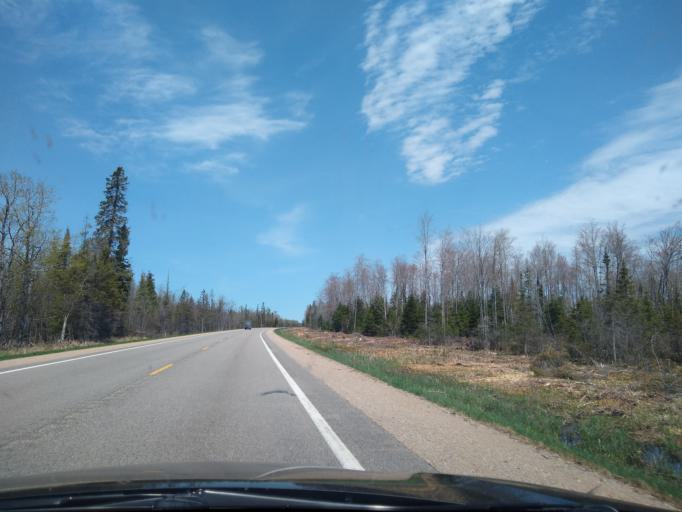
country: US
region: Michigan
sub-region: Delta County
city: Gladstone
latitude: 46.0362
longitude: -86.9812
